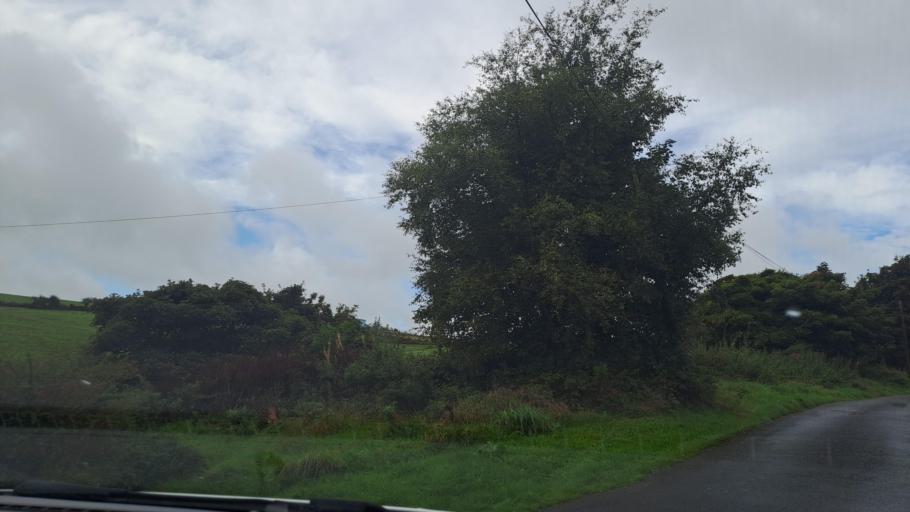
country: IE
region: Ulster
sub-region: An Cabhan
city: Kingscourt
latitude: 53.9483
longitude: -6.8566
